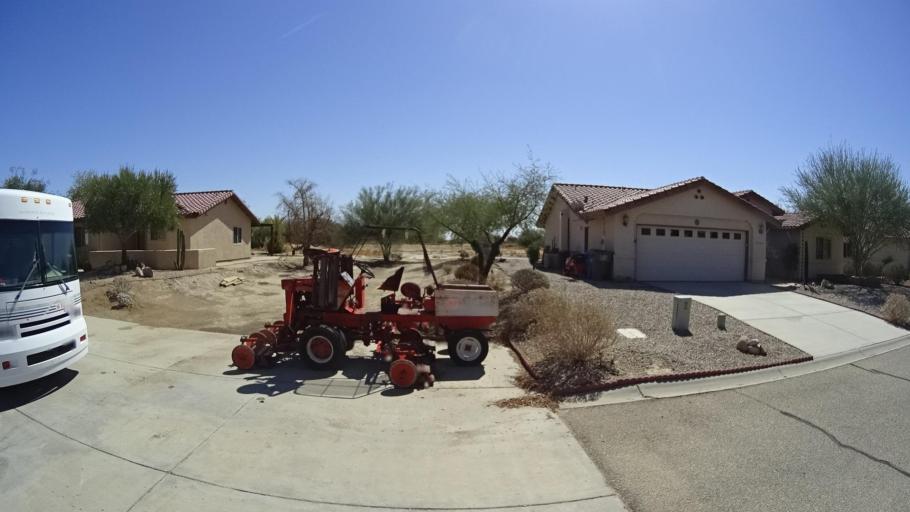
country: US
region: California
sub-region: San Diego County
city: Borrego Springs
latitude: 33.2423
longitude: -116.3535
